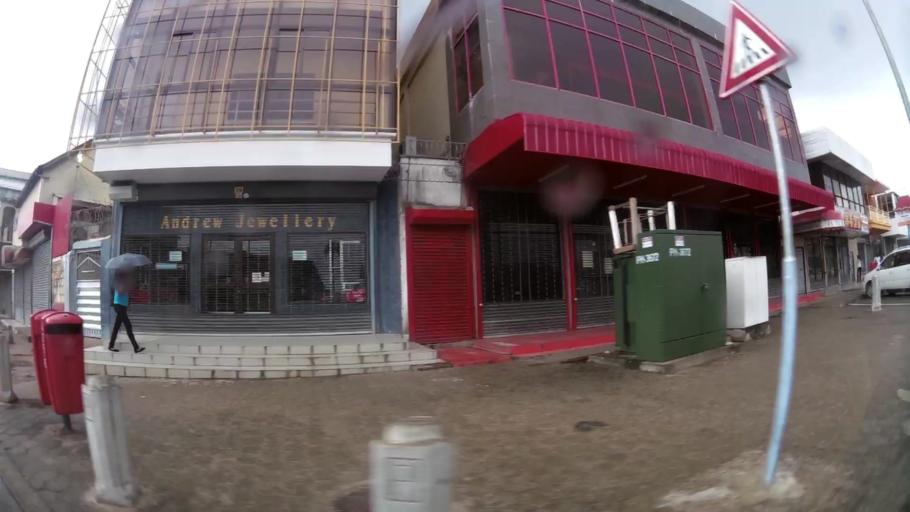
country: SR
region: Paramaribo
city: Paramaribo
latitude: 5.8247
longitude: -55.1617
